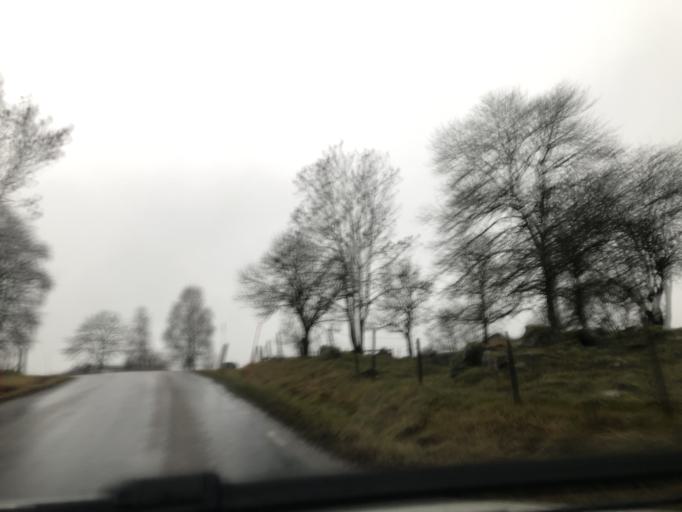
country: SE
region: Vaestra Goetaland
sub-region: Ulricehamns Kommun
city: Ulricehamn
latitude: 57.8488
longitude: 13.5424
